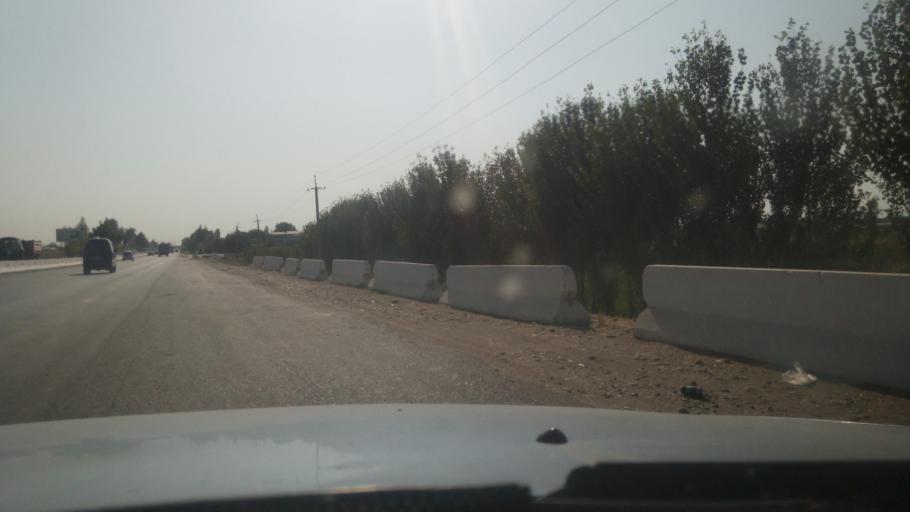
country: UZ
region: Toshkent
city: Urtaowul
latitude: 41.2148
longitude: 69.1278
